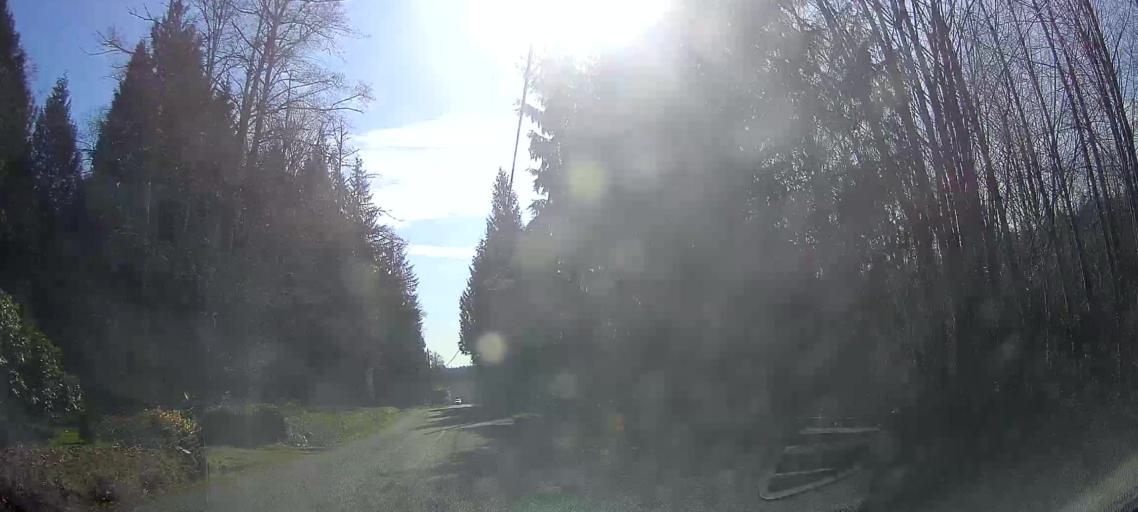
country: US
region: Washington
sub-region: Whatcom County
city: Sudden Valley
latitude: 48.6011
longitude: -122.3665
